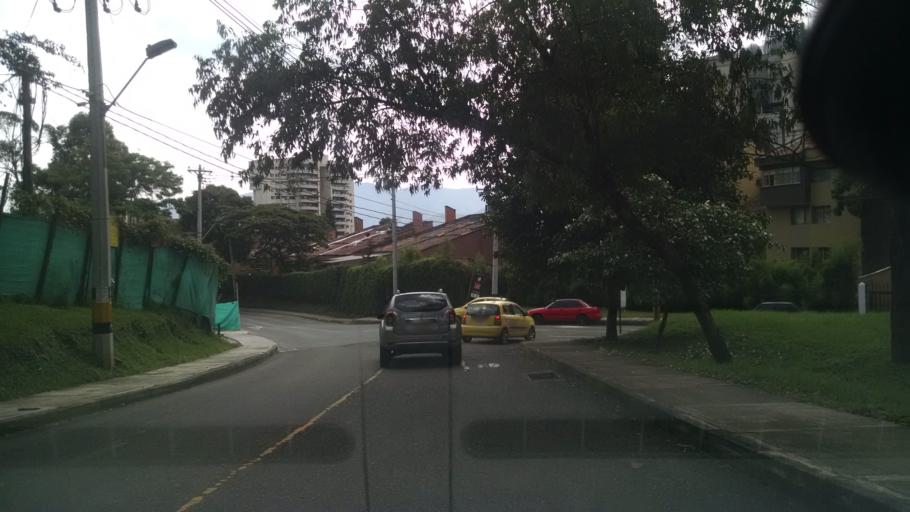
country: CO
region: Antioquia
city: Envigado
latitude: 6.1988
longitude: -75.5673
